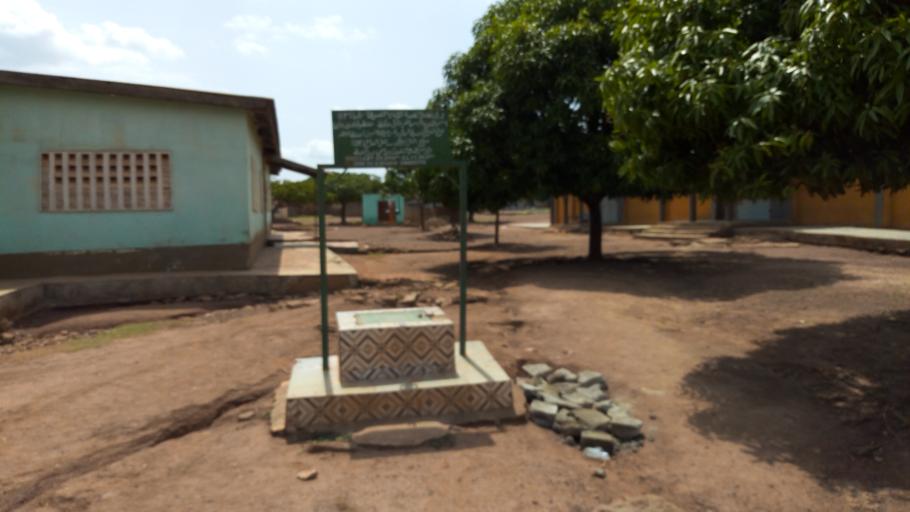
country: CI
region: Vallee du Bandama
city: Bouake
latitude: 7.7174
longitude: -5.0220
